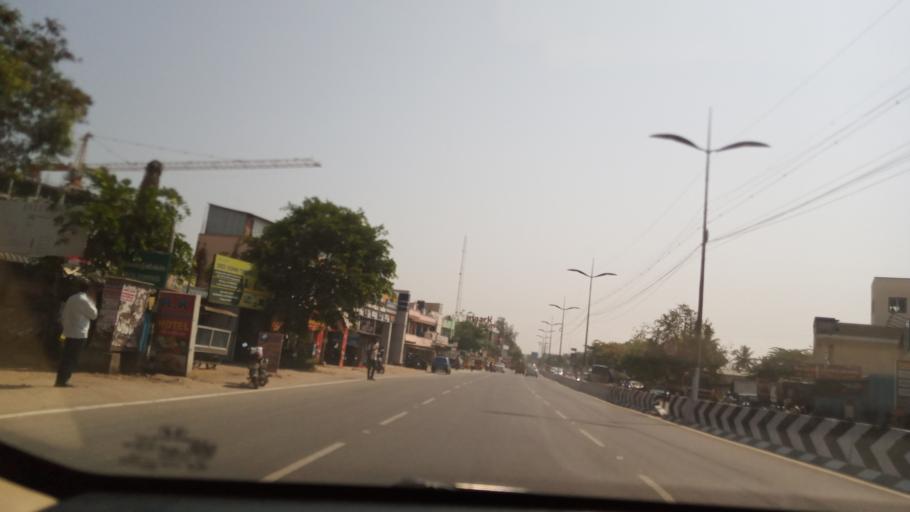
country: IN
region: Tamil Nadu
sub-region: Coimbatore
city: Irugur
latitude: 11.0447
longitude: 77.0481
